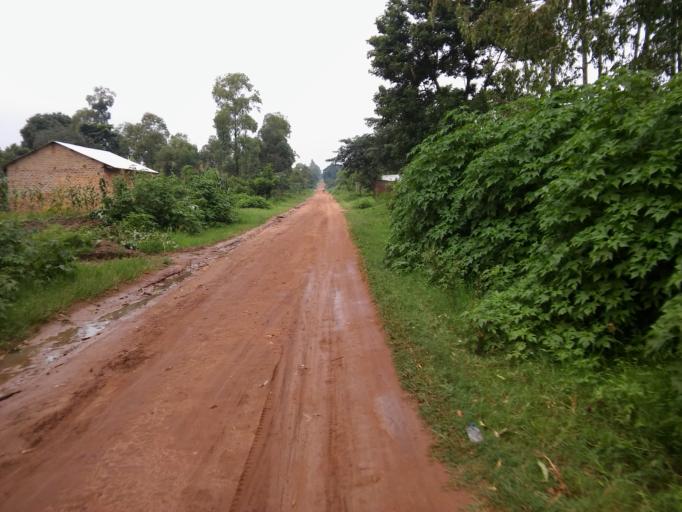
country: UG
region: Eastern Region
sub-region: Mbale District
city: Mbale
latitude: 0.9985
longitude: 34.1940
